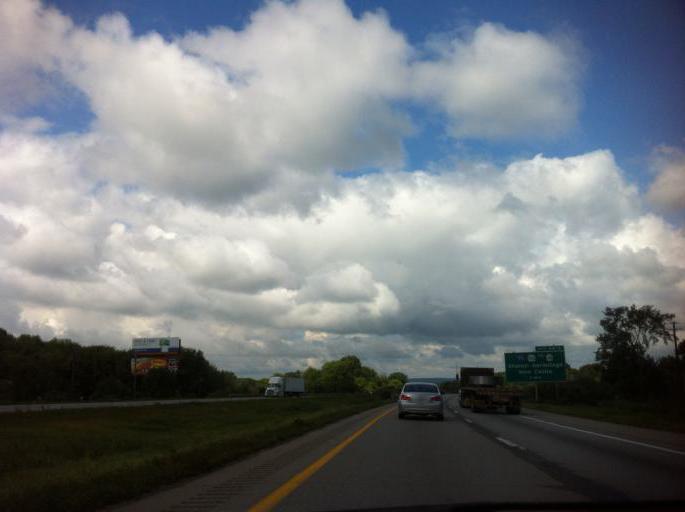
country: US
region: Pennsylvania
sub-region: Mercer County
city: Hermitage
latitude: 41.1830
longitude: -80.4191
